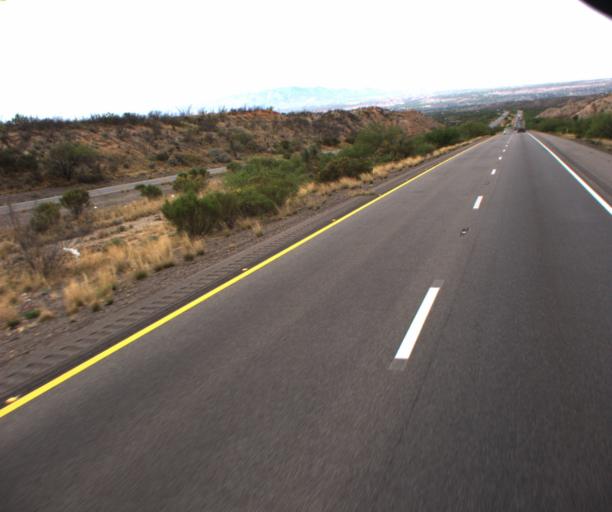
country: US
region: Arizona
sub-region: Cochise County
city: Saint David
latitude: 31.9827
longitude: -110.2081
